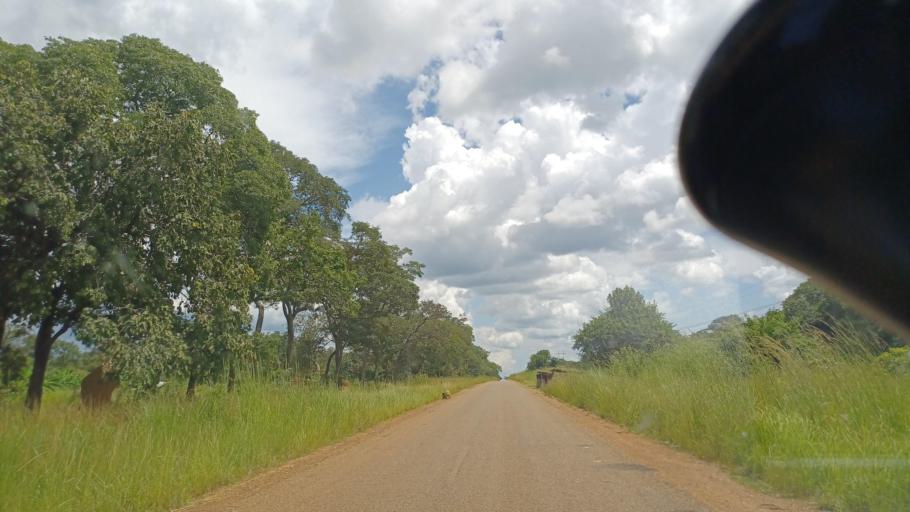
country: ZM
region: North-Western
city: Solwezi
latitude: -12.7037
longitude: 26.0330
